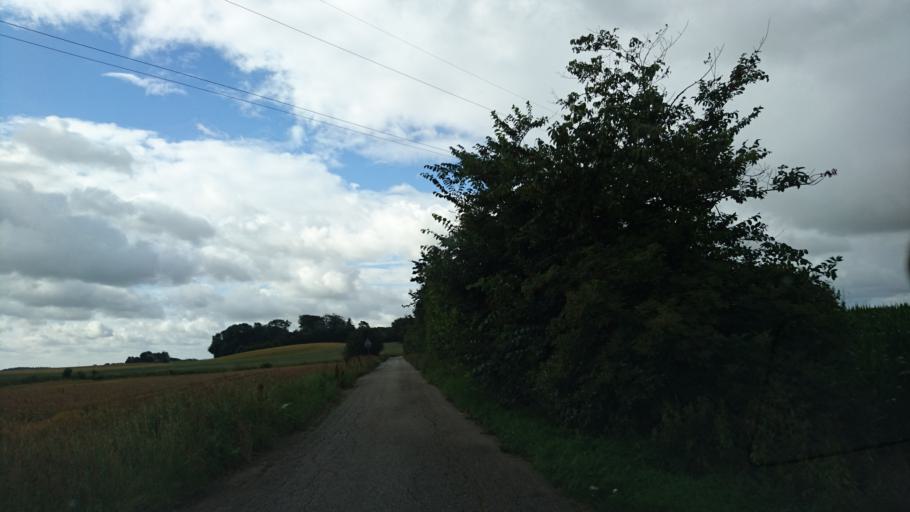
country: DK
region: North Denmark
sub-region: Hjorring Kommune
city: Sindal
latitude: 57.3819
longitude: 10.2445
